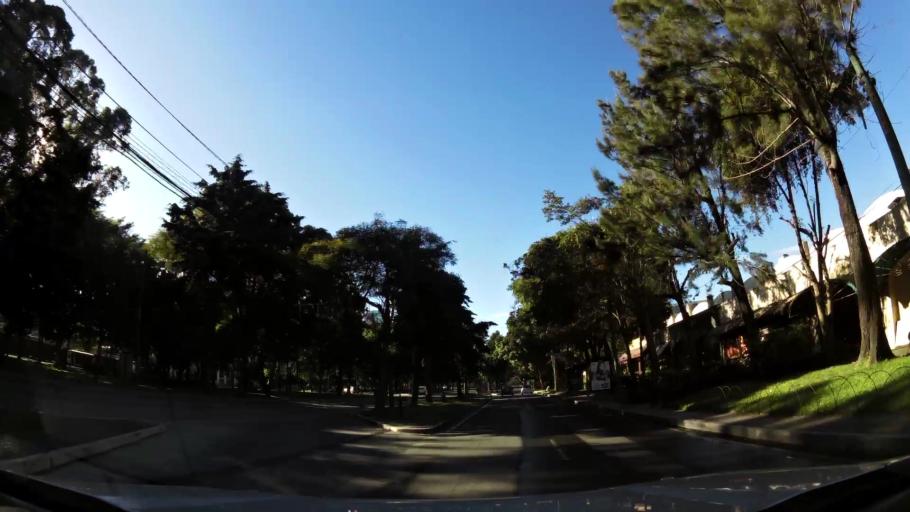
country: GT
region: Guatemala
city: Santa Catarina Pinula
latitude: 14.5994
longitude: -90.5171
